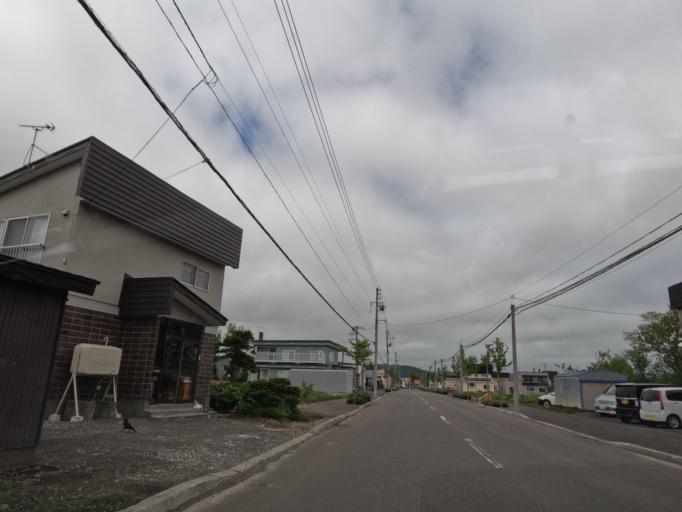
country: JP
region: Hokkaido
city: Tobetsu
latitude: 43.2352
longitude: 141.5143
